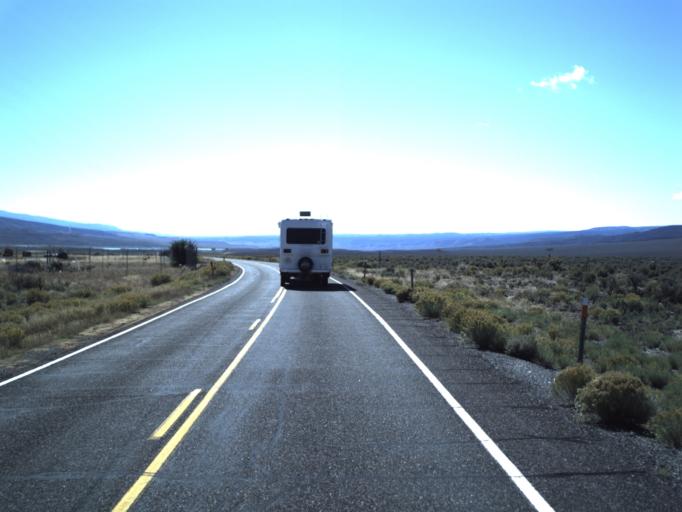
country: US
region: Utah
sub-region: Piute County
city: Junction
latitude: 38.2719
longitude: -111.9865
